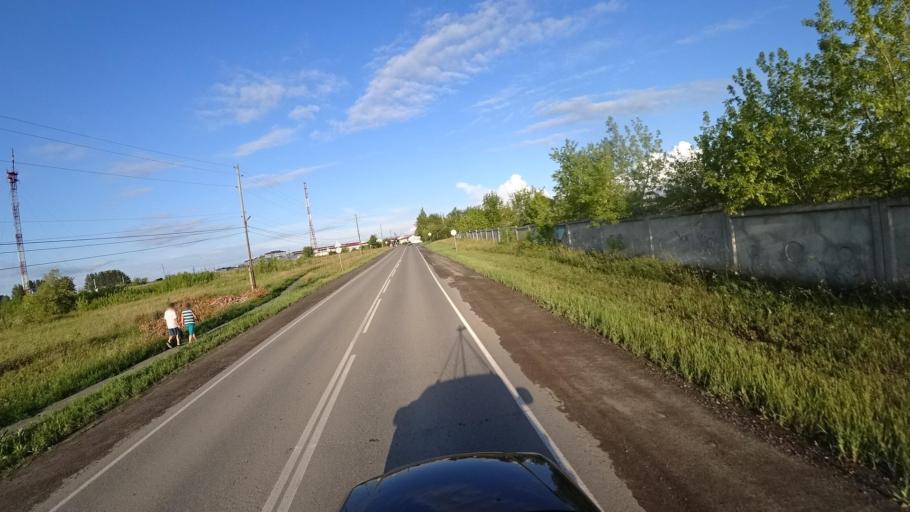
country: RU
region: Sverdlovsk
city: Kamyshlov
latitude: 56.8576
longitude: 62.7266
